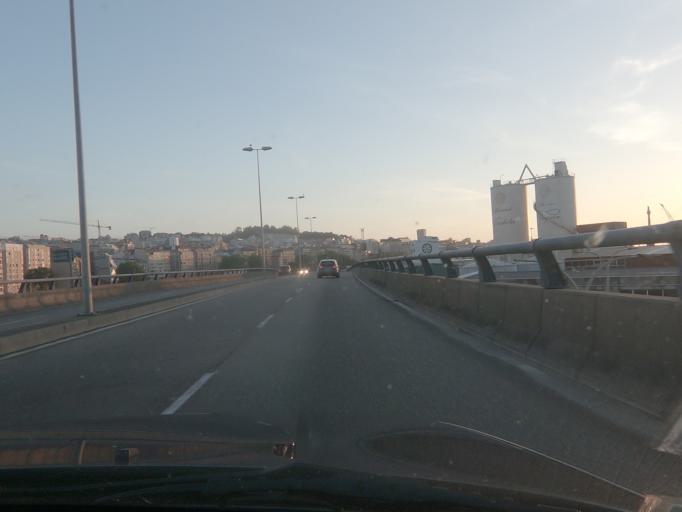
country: ES
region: Galicia
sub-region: Provincia de Pontevedra
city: Vigo
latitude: 42.2423
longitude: -8.7079
